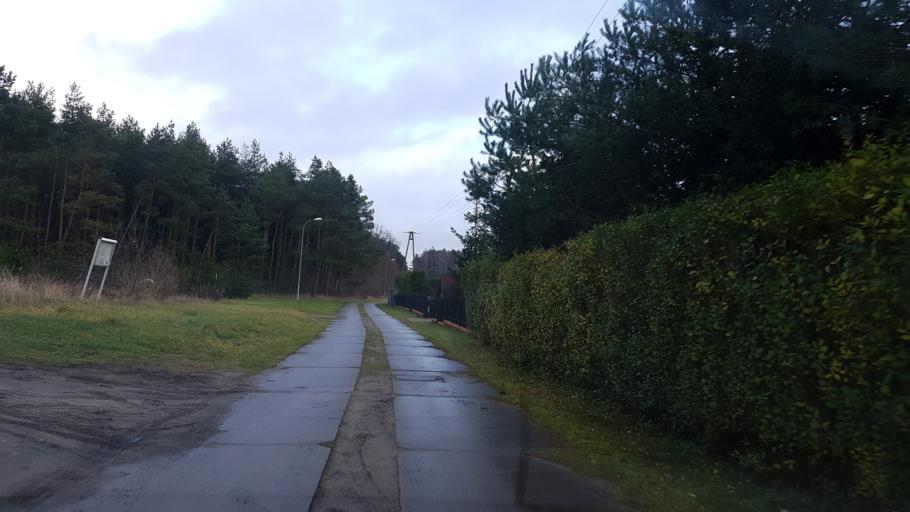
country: PL
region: West Pomeranian Voivodeship
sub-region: Powiat kolobrzeski
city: Grzybowo
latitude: 54.1092
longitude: 15.5314
